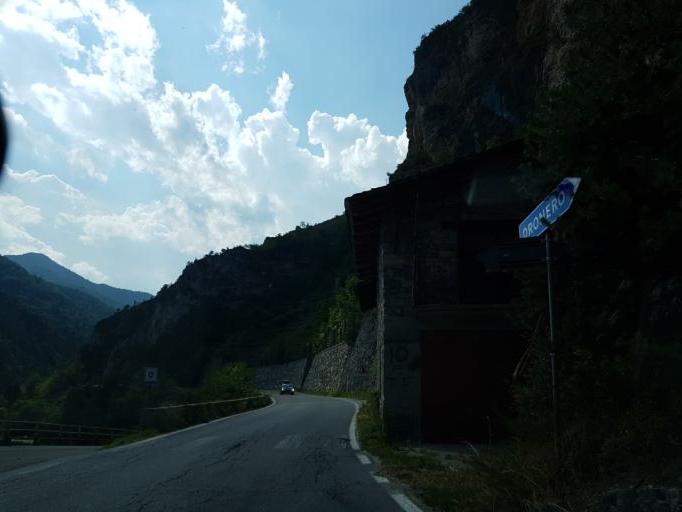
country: IT
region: Piedmont
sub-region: Provincia di Cuneo
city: Macra
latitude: 44.5003
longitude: 7.1777
